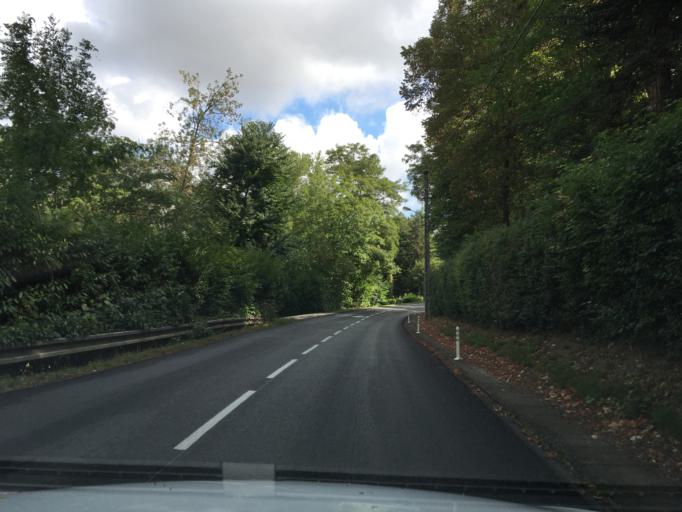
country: FR
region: Aquitaine
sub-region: Departement du Lot-et-Garonne
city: Le Passage
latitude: 44.2178
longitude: 0.6097
